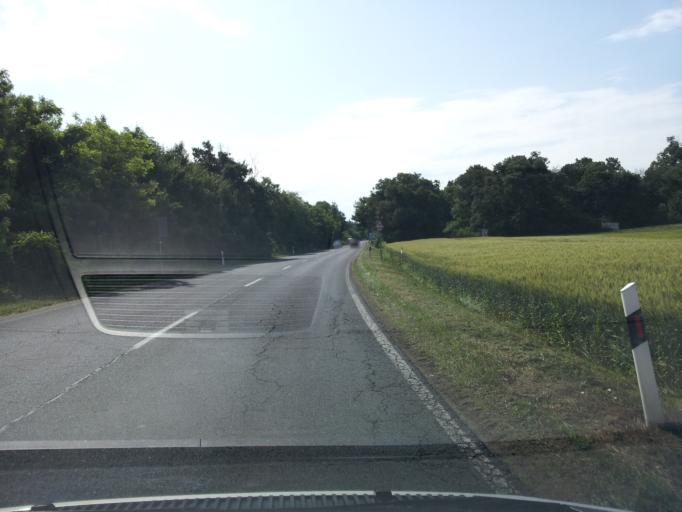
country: HU
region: Veszprem
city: Csopak
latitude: 47.0206
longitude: 17.9103
